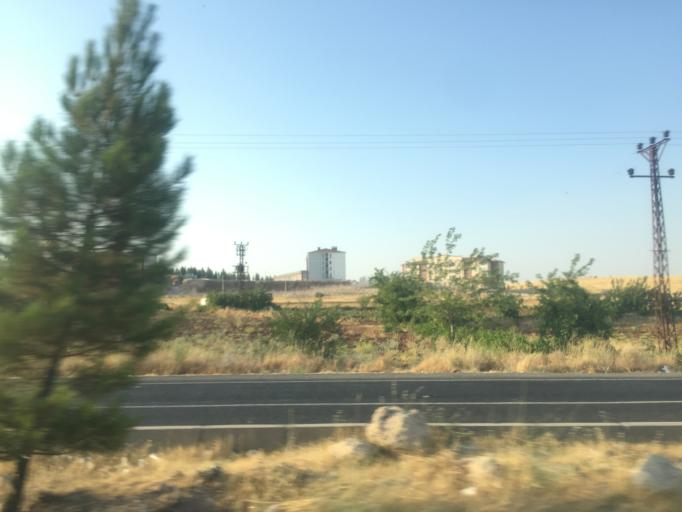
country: TR
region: Mardin
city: Acirli
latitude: 37.4373
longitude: 41.3075
